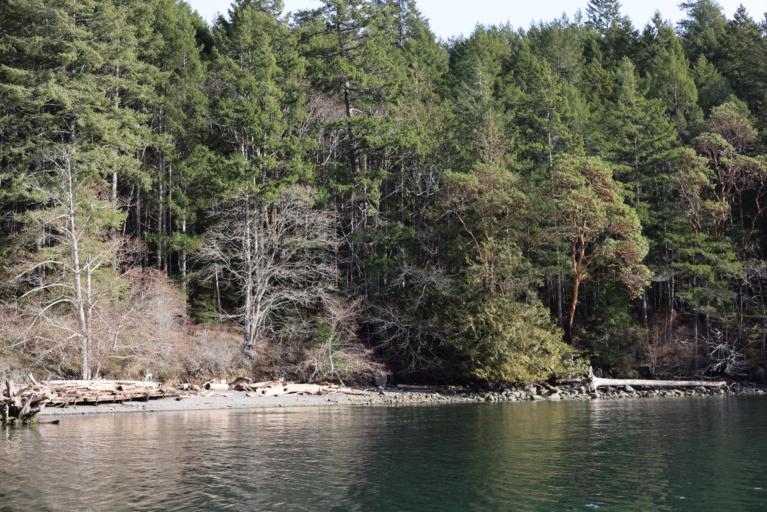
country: CA
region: British Columbia
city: Duncan
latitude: 48.7647
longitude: -123.5969
